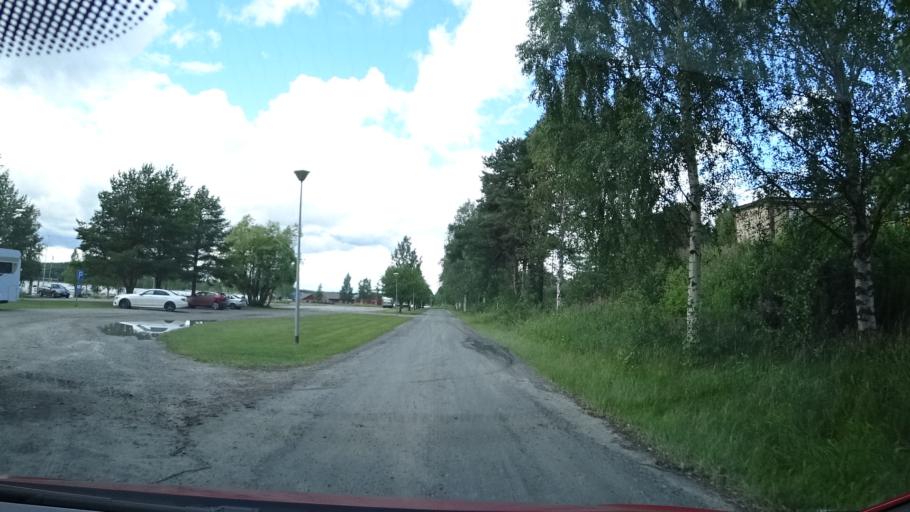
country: FI
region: North Karelia
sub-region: Pielisen Karjala
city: Nurmes
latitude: 63.5423
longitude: 29.1328
